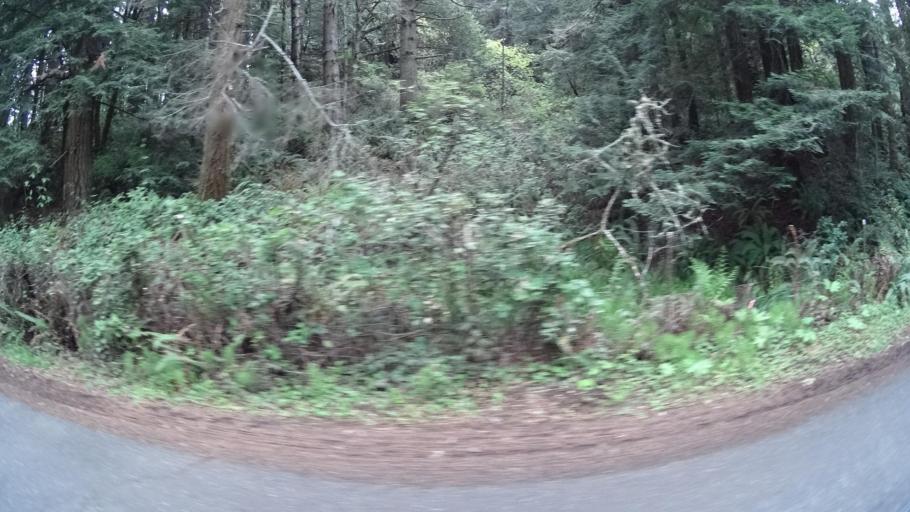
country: US
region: California
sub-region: Humboldt County
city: Blue Lake
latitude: 40.8235
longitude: -124.0000
